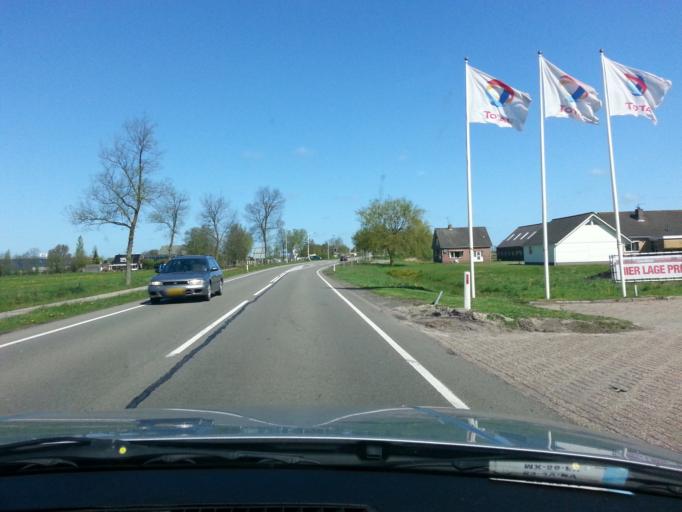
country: NL
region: Friesland
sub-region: Gemeente Achtkarspelen
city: Augustinusga
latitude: 53.2238
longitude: 6.1745
